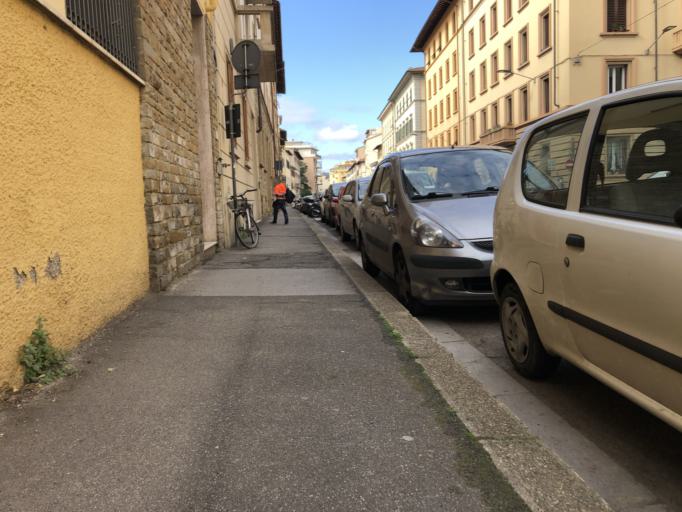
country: IT
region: Tuscany
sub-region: Province of Florence
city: Florence
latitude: 43.7751
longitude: 11.2752
